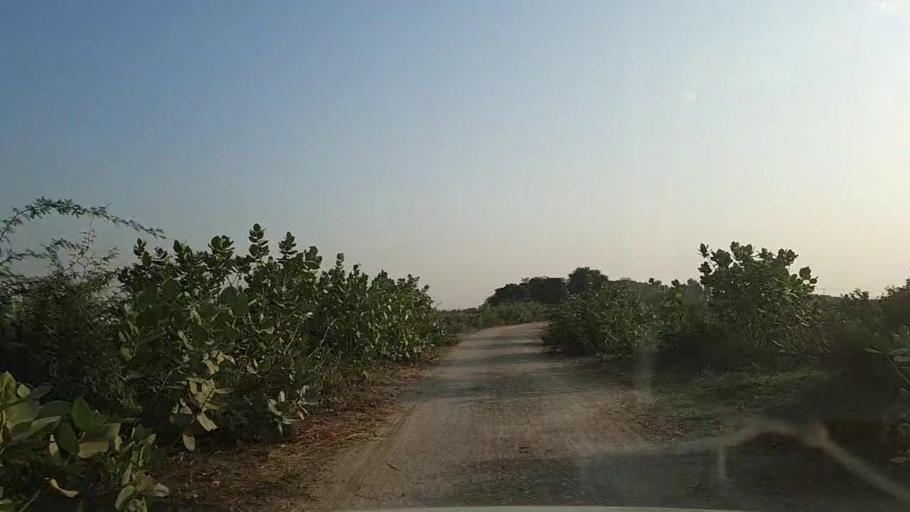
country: PK
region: Sindh
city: Daro Mehar
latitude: 24.7671
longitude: 68.1935
